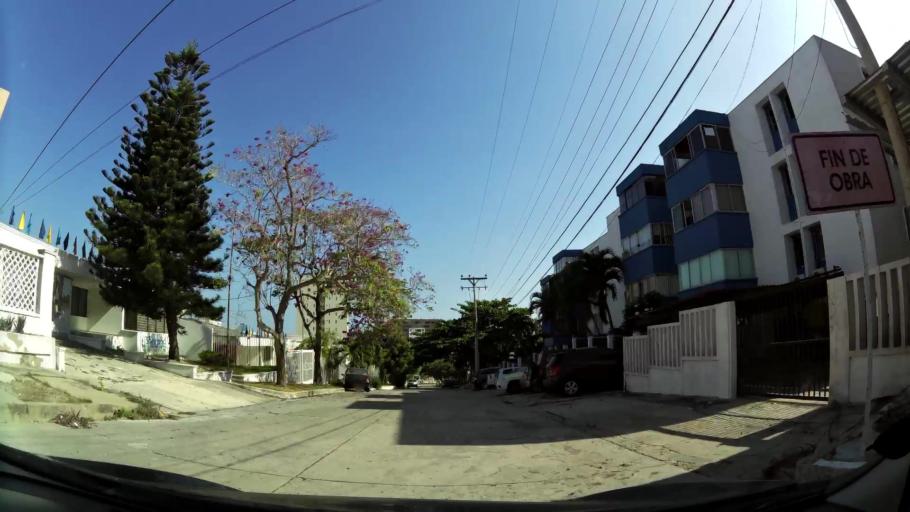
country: CO
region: Atlantico
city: Barranquilla
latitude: 10.9979
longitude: -74.8265
